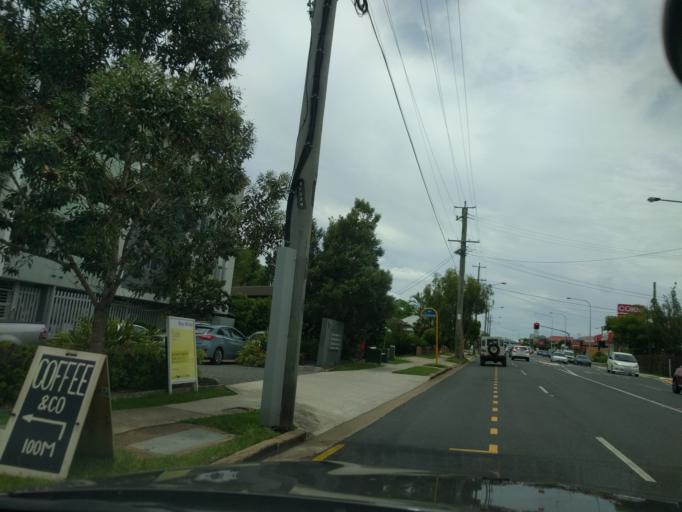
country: AU
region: Queensland
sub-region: Brisbane
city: Grange
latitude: -27.4226
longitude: 152.9997
